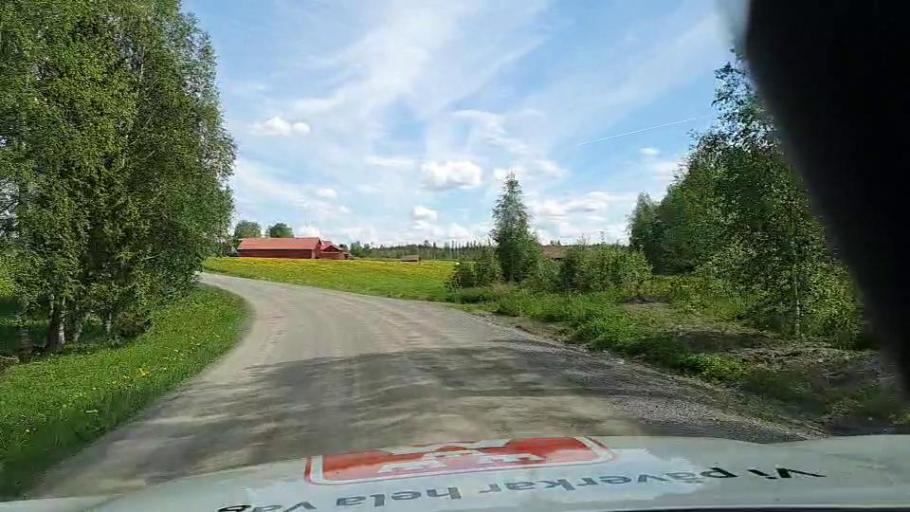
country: SE
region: Jaemtland
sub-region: OEstersunds Kommun
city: Brunflo
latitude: 63.0038
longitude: 14.7951
